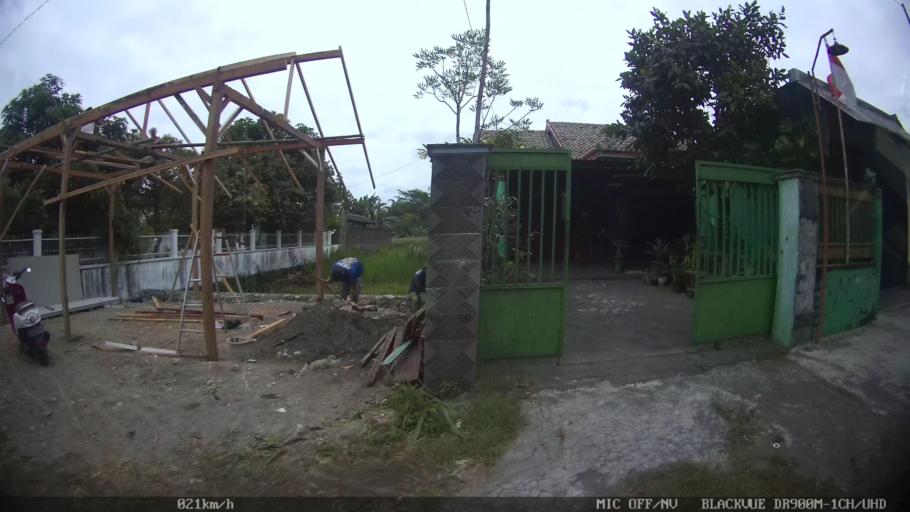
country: ID
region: Daerah Istimewa Yogyakarta
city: Sewon
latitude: -7.8567
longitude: 110.3961
